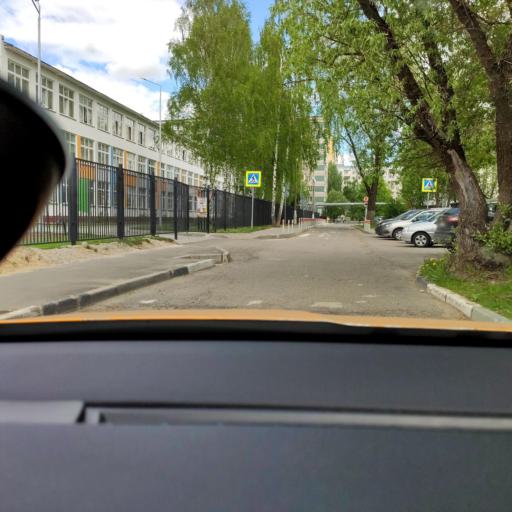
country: RU
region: Moskovskaya
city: Novopodrezkovo
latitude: 55.9411
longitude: 37.3440
